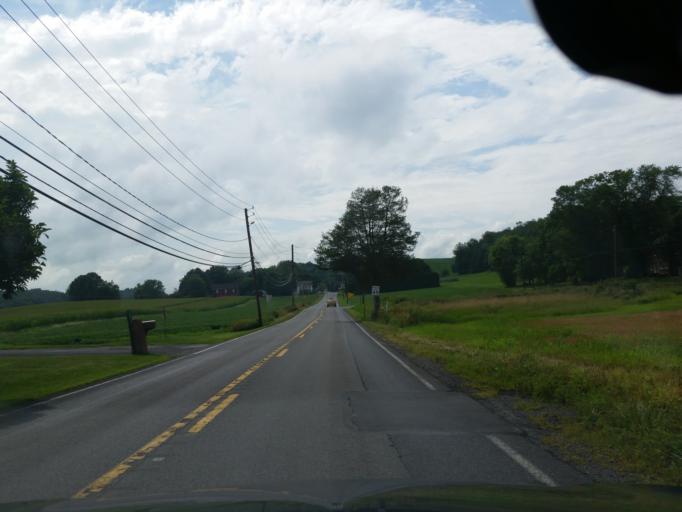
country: US
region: Pennsylvania
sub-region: Union County
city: New Columbia
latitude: 41.0193
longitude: -76.8814
